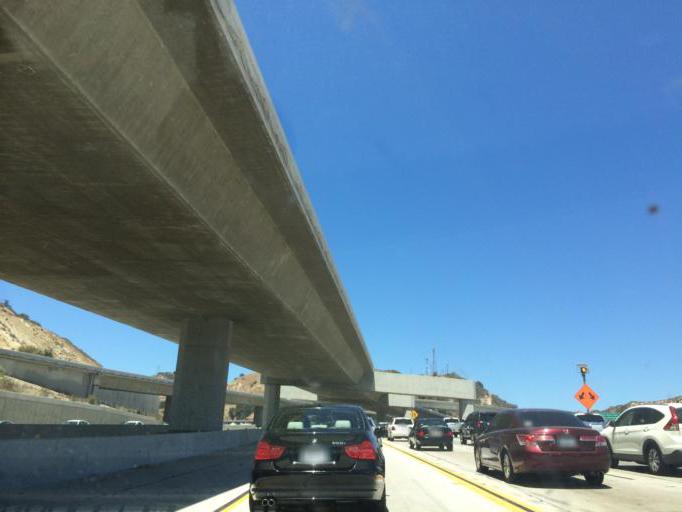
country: US
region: California
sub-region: Los Angeles County
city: Santa Clarita
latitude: 34.3322
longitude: -118.5070
